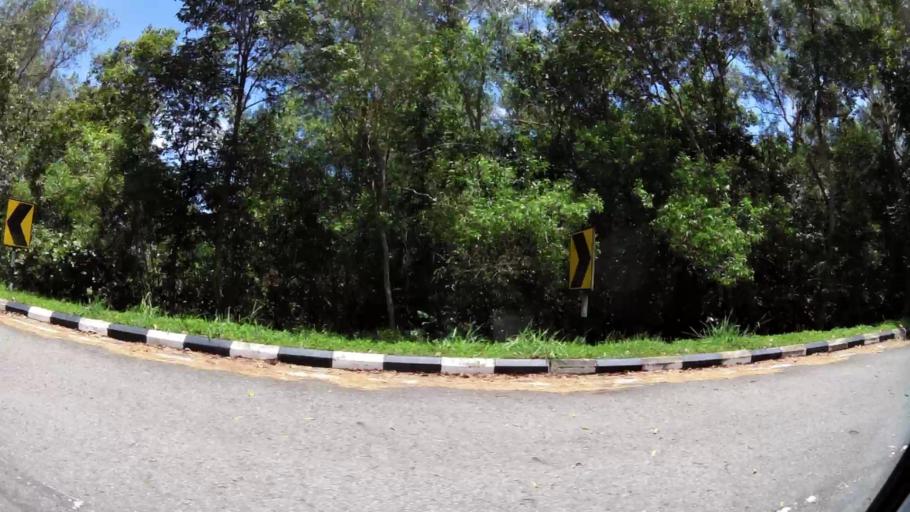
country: BN
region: Brunei and Muara
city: Bandar Seri Begawan
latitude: 4.9235
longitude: 114.9591
